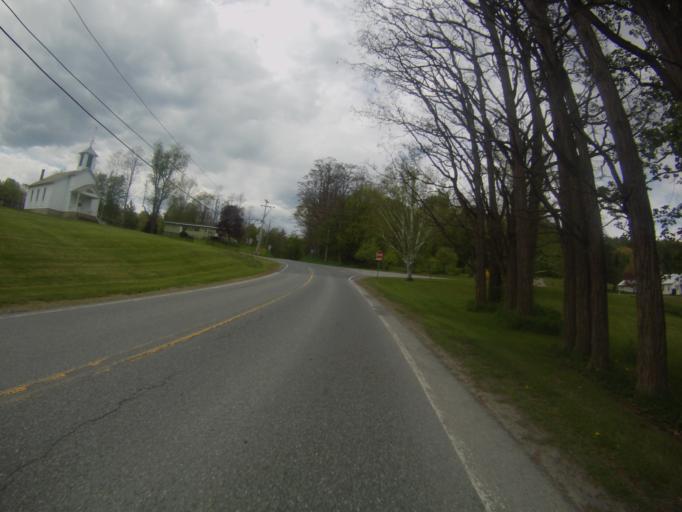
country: US
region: New York
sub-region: Essex County
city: Port Henry
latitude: 43.9566
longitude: -73.4861
